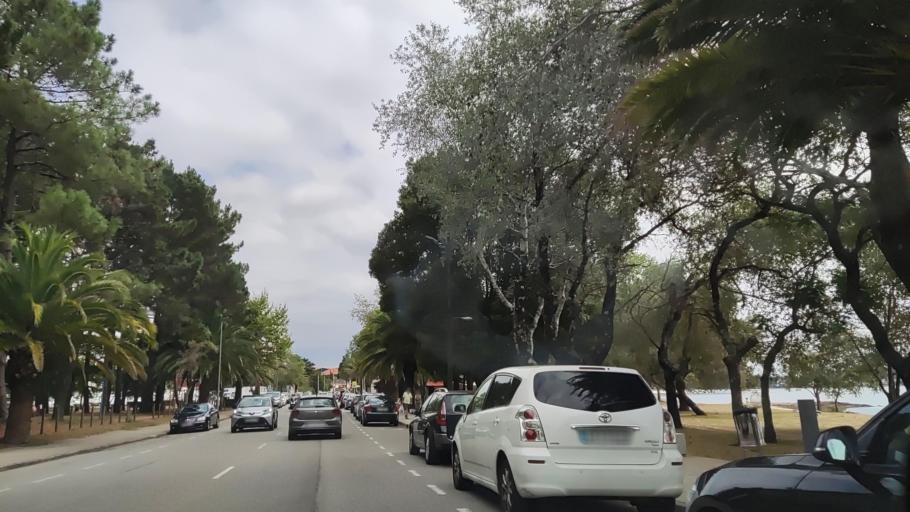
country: ES
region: Galicia
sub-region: Provincia da Coruna
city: Boiro
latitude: 42.6411
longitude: -8.8984
